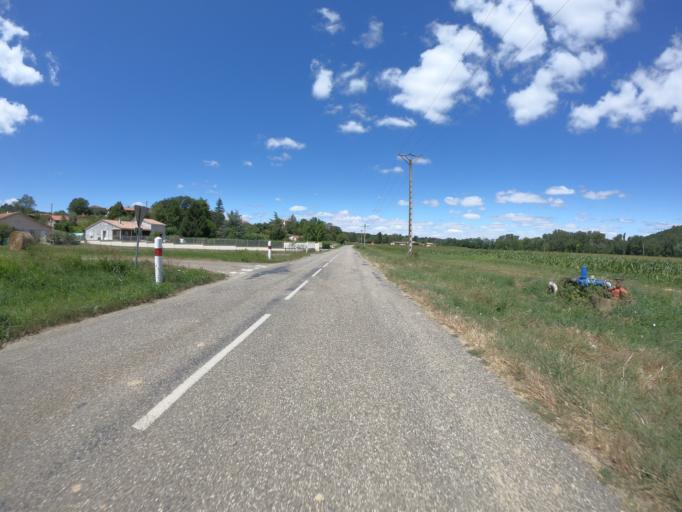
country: FR
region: Midi-Pyrenees
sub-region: Departement de l'Ariege
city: Verniolle
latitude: 43.0621
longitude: 1.7400
